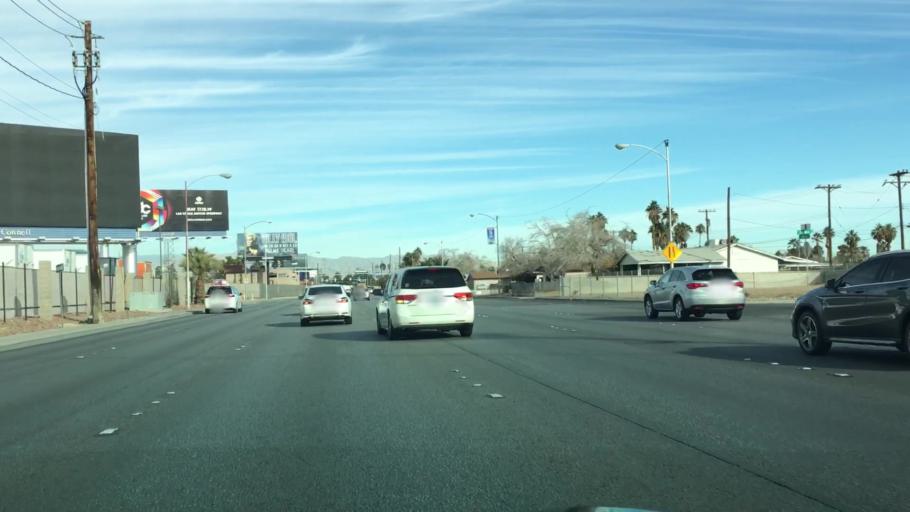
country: US
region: Nevada
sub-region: Clark County
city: Paradise
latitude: 36.0952
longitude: -115.1460
